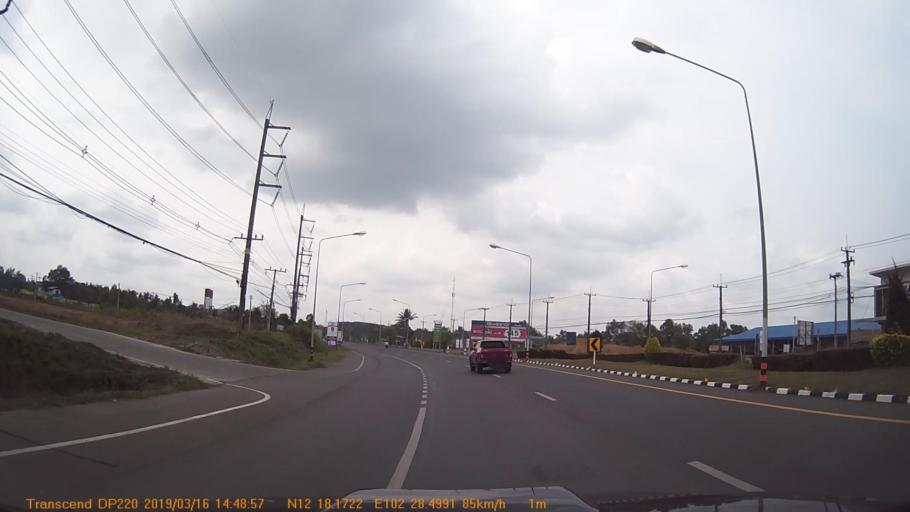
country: TH
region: Trat
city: Khao Saming
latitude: 12.3033
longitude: 102.4748
